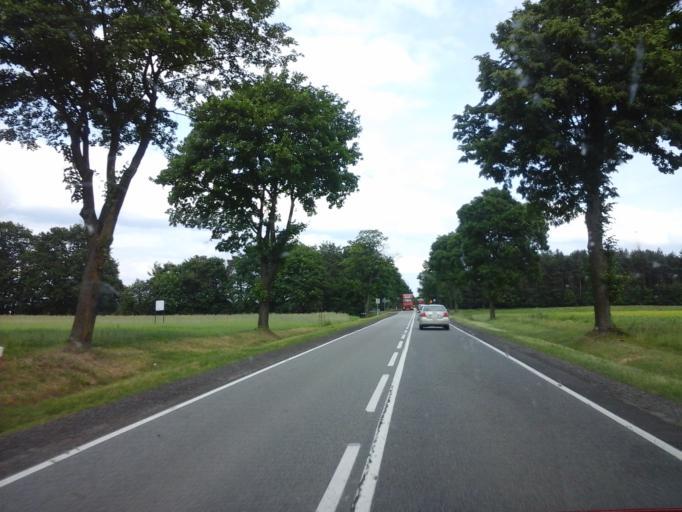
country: PL
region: Lodz Voivodeship
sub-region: Powiat opoczynski
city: Paradyz
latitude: 51.3124
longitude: 20.0811
